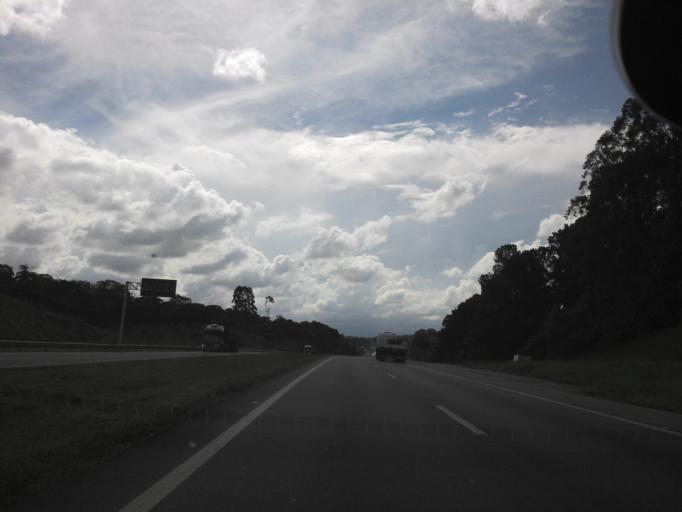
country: BR
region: Sao Paulo
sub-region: Itatiba
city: Itatiba
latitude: -22.9473
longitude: -46.8702
